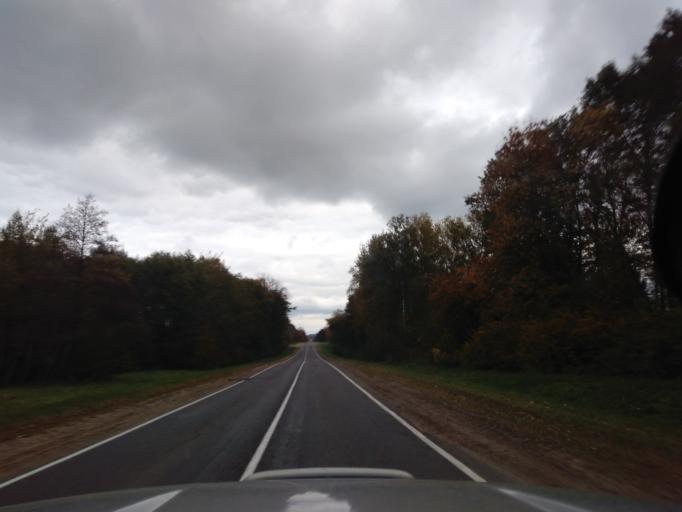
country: BY
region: Minsk
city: Slutsk
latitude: 53.2223
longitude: 27.3707
